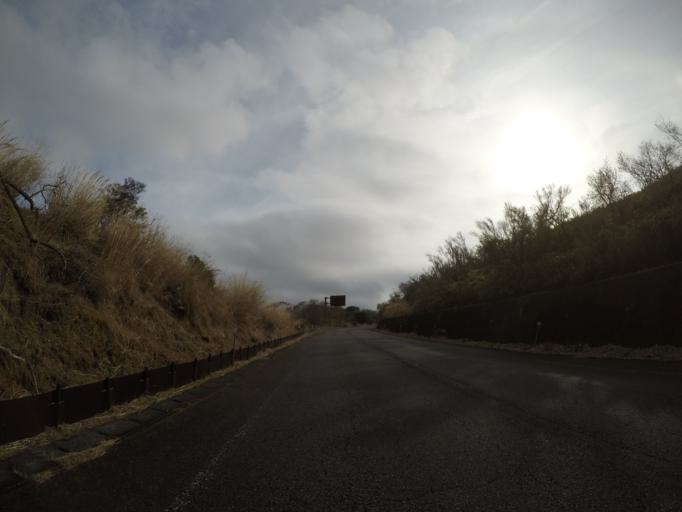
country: JP
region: Shizuoka
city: Heda
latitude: 34.8703
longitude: 138.8393
